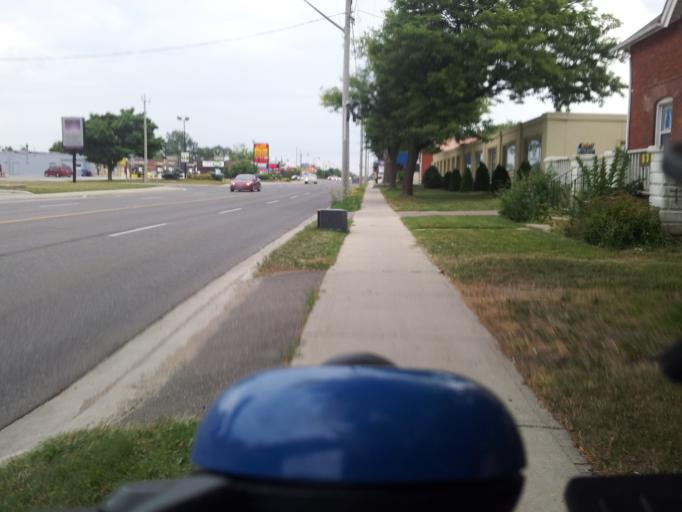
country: CA
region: Ontario
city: Stratford
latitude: 43.3710
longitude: -80.9608
